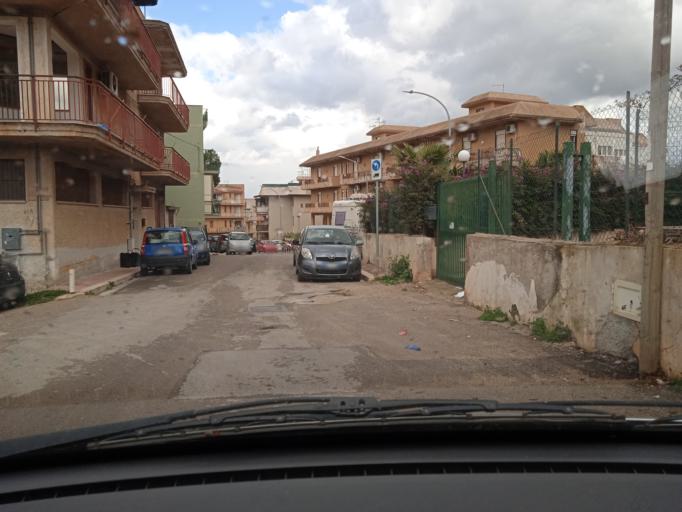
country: IT
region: Sicily
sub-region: Palermo
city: Villabate
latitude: 38.0743
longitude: 13.4400
